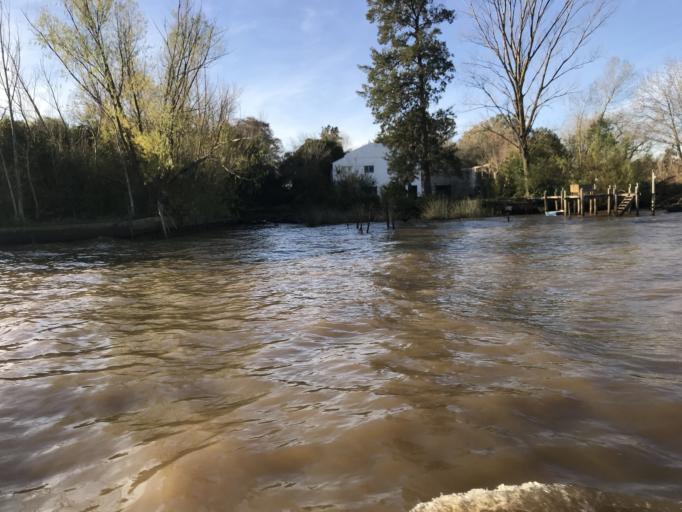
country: AR
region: Buenos Aires
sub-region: Partido de Tigre
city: Tigre
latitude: -34.4142
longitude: -58.5817
